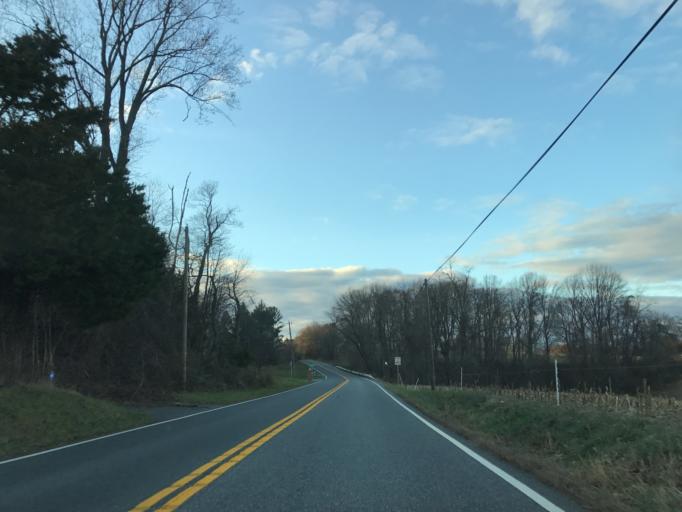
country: US
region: Pennsylvania
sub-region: York County
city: Susquehanna Trails
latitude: 39.7060
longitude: -76.2570
